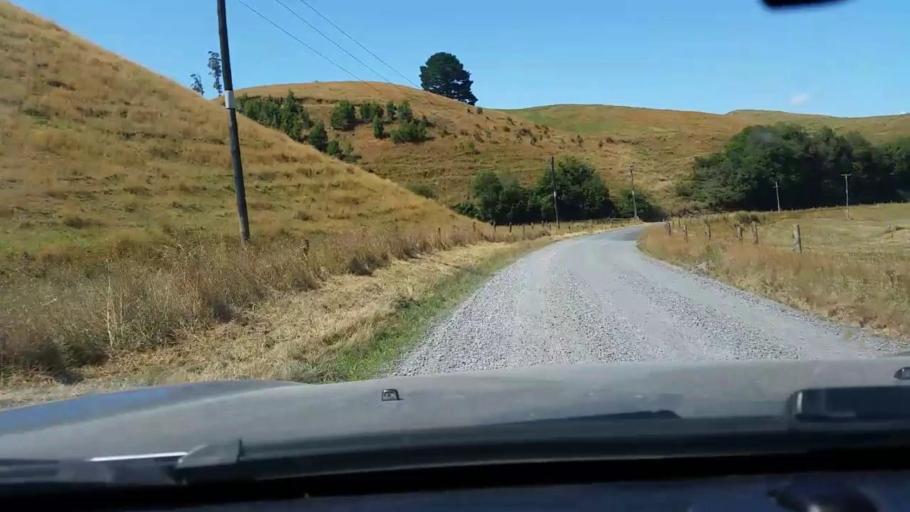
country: NZ
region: Bay of Plenty
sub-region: Rotorua District
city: Rotorua
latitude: -38.3849
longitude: 176.1158
